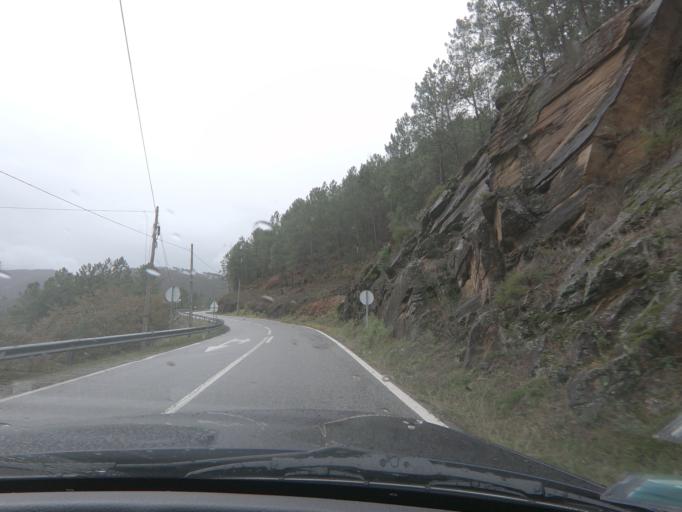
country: PT
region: Vila Real
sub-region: Mondim de Basto
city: Mondim de Basto
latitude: 41.3660
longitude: -7.9196
